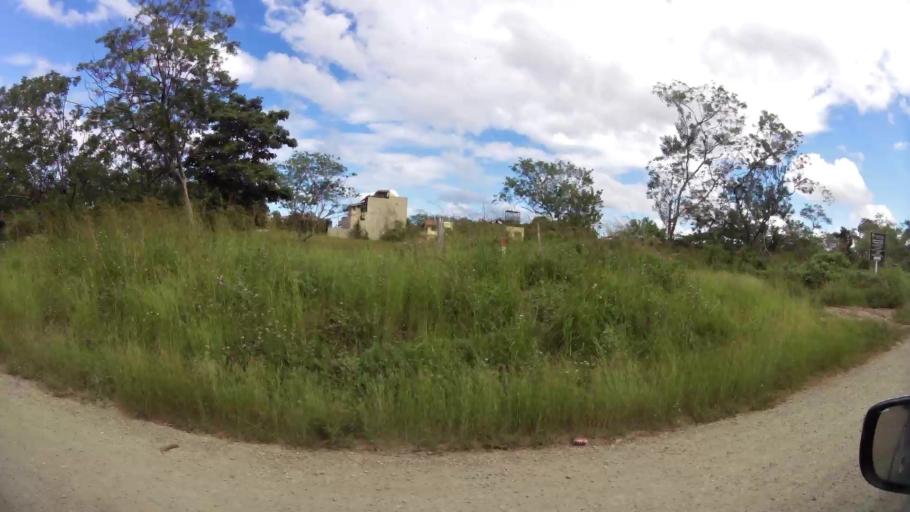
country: CR
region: Guanacaste
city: Santa Cruz
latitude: 10.2867
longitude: -85.8496
